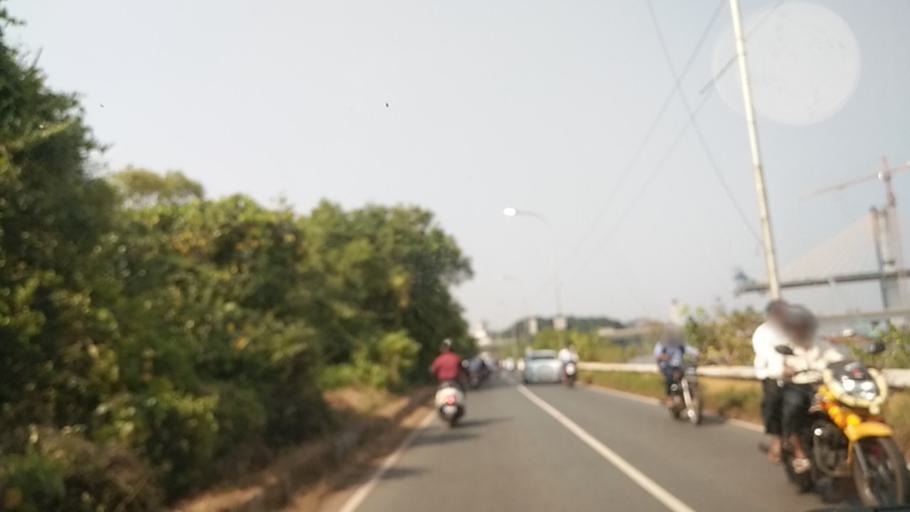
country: IN
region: Goa
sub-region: North Goa
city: Panaji
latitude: 15.4996
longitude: 73.8409
